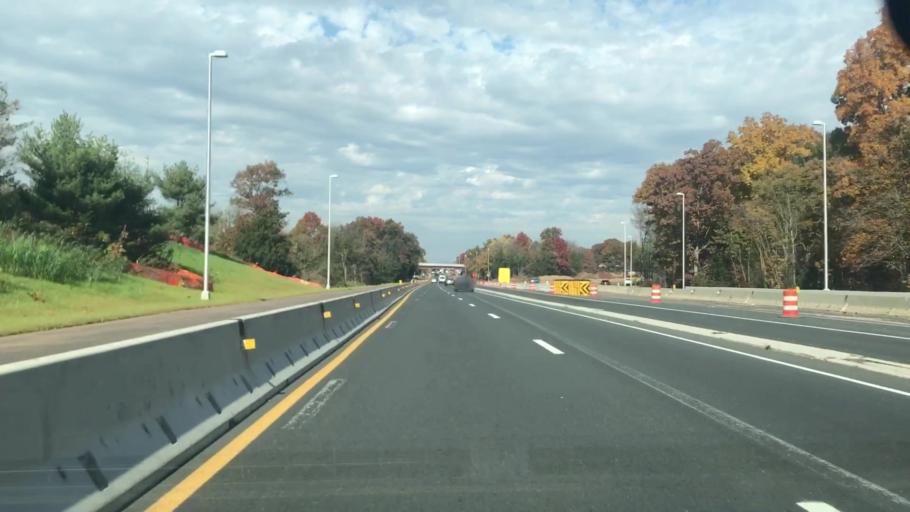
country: US
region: New Jersey
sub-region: Somerset County
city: Bridgewater
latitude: 40.6373
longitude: -74.6441
